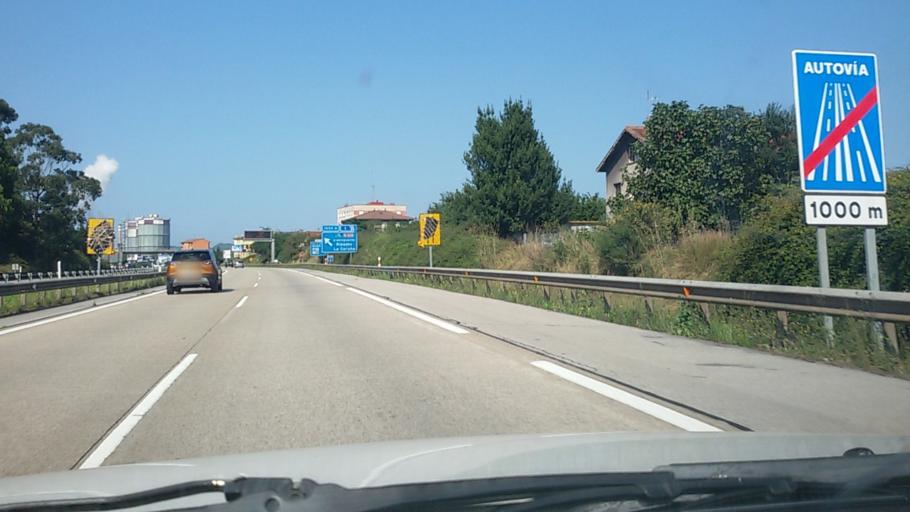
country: ES
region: Asturias
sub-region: Province of Asturias
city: Aviles
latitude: 43.5521
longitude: -5.8824
